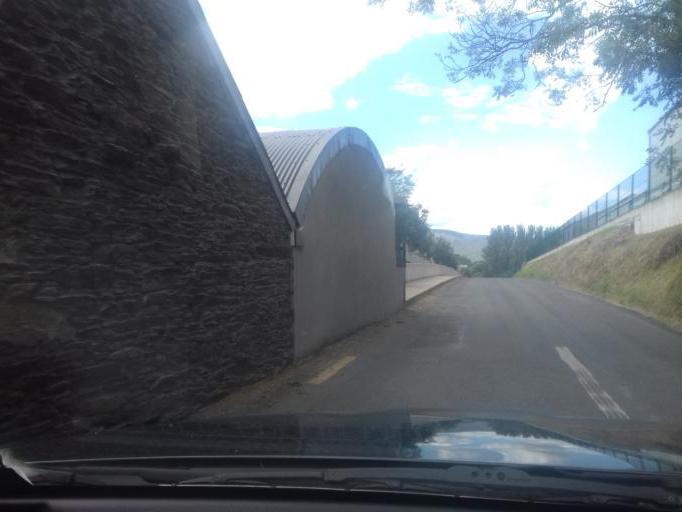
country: IE
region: Munster
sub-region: Waterford
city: Portlaw
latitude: 52.2105
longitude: -7.4254
